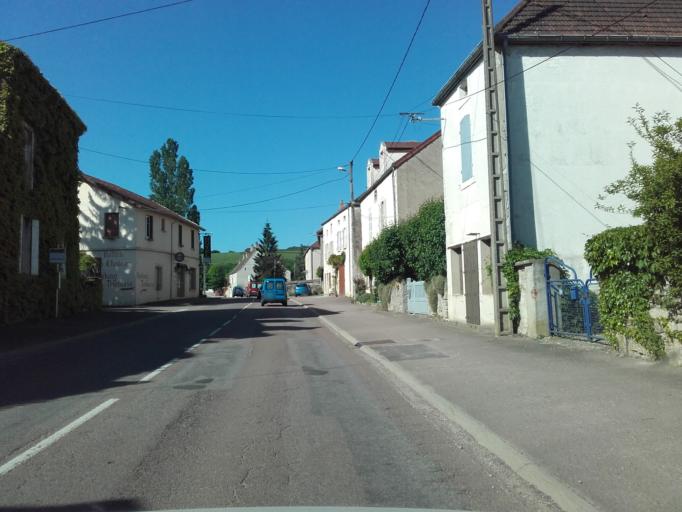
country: FR
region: Bourgogne
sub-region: Departement de la Cote-d'Or
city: Nolay
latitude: 46.9562
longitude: 4.6763
